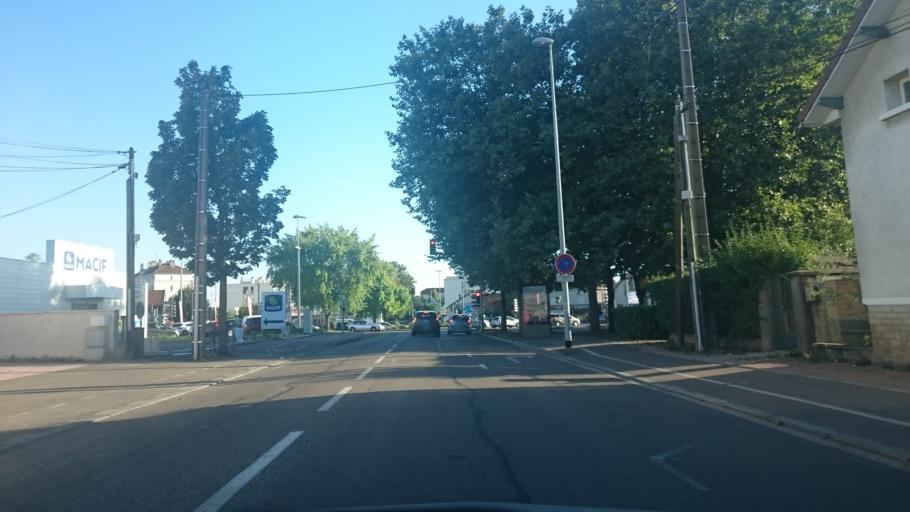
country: FR
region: Bourgogne
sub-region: Departement de la Cote-d'Or
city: Saint-Apollinaire
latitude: 47.3375
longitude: 5.0566
